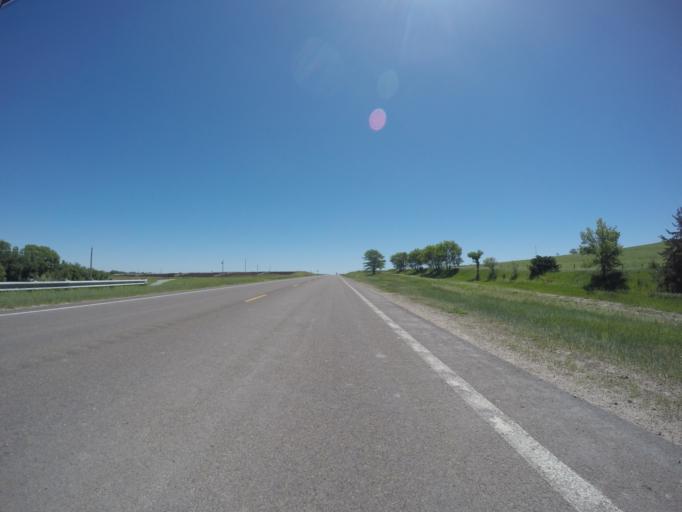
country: US
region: Kansas
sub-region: Phillips County
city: Phillipsburg
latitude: 39.8286
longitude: -99.5920
